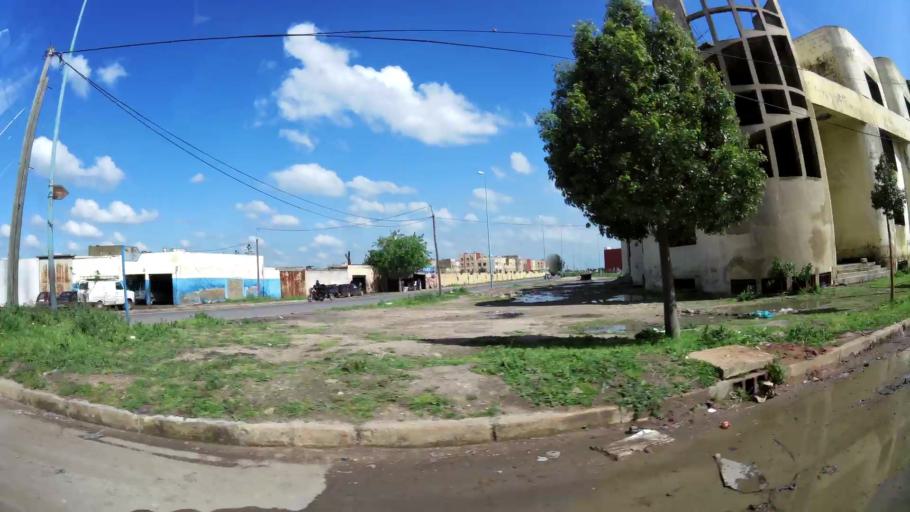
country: MA
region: Grand Casablanca
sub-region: Mediouna
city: Mediouna
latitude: 33.4490
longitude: -7.5180
